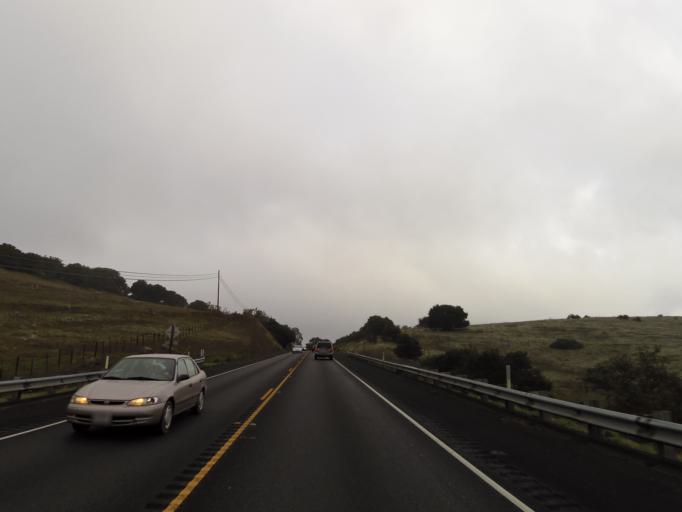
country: US
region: California
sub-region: Marin County
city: Black Point-Green Point
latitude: 38.1821
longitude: -122.4437
